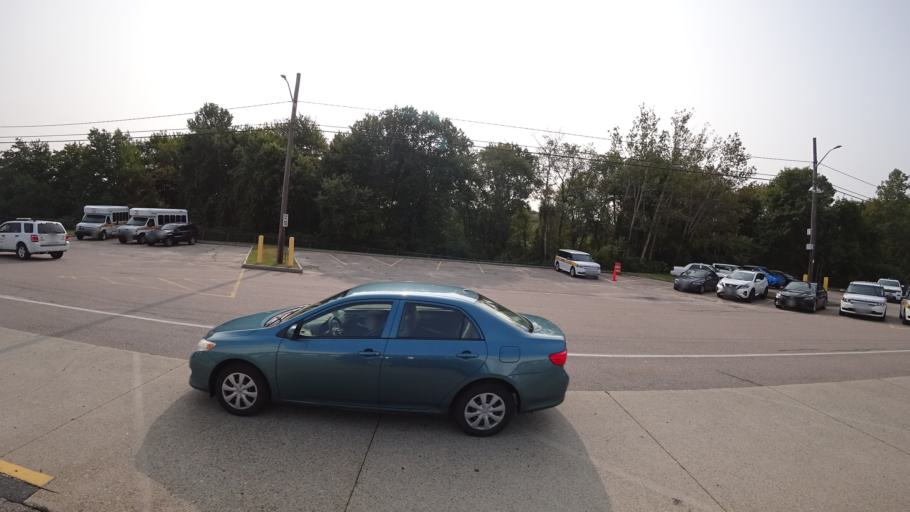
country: US
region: Massachusetts
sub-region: Norfolk County
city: Dedham
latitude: 42.2295
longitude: -71.1323
